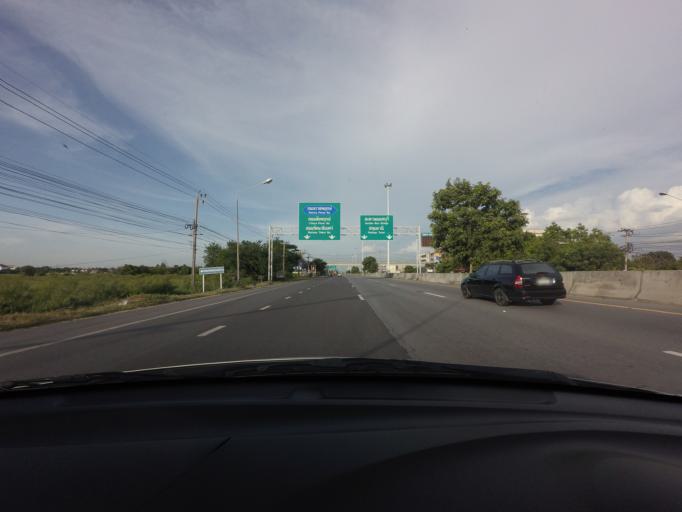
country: TH
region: Nonthaburi
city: Bang Bua Thong
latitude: 13.9495
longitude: 100.4511
